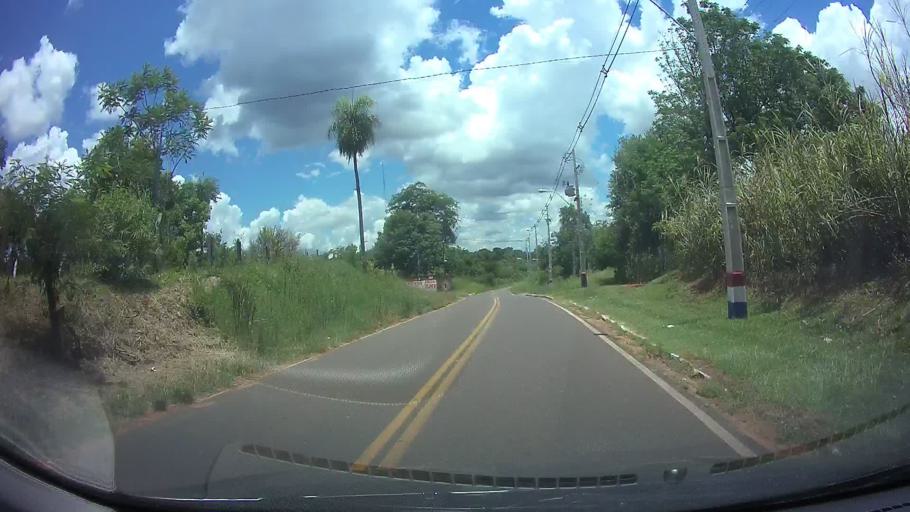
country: PY
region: Central
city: Capiata
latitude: -25.3148
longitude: -57.4318
